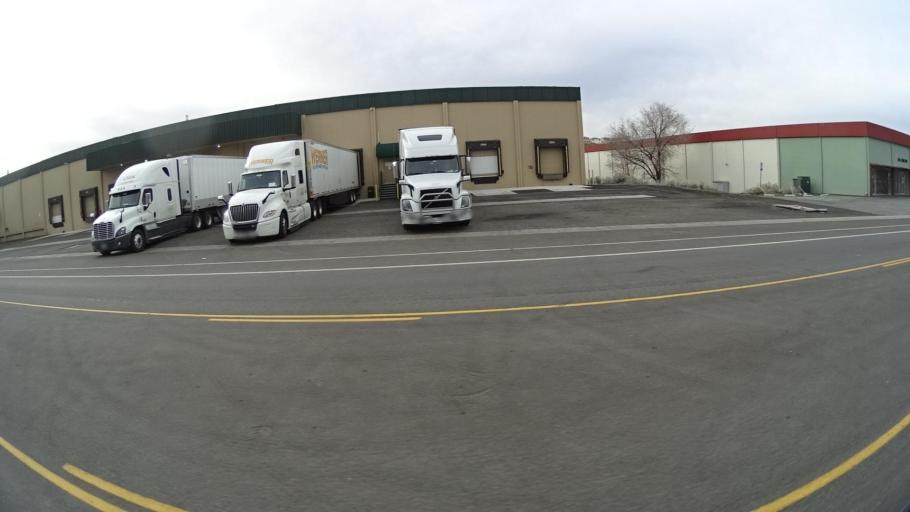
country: US
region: Nevada
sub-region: Washoe County
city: Reno
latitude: 39.5702
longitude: -119.8156
